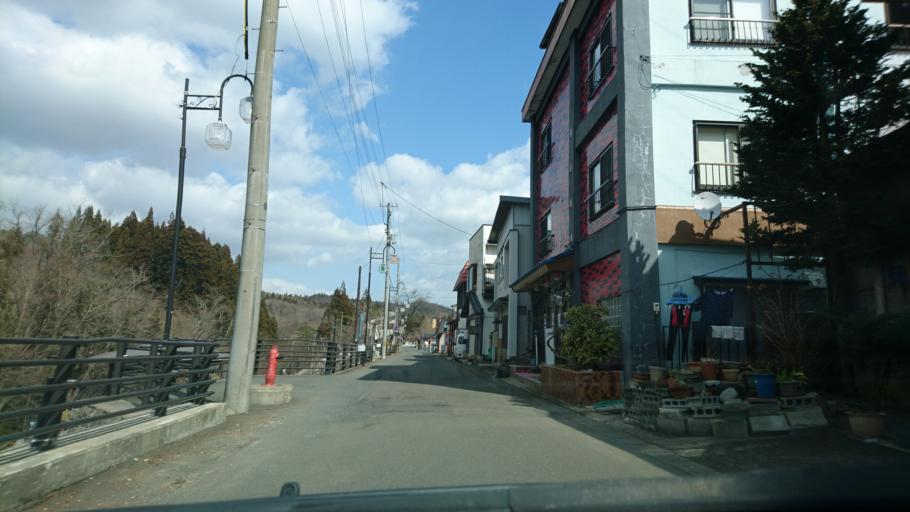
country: JP
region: Iwate
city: Shizukuishi
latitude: 39.6364
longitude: 140.9231
